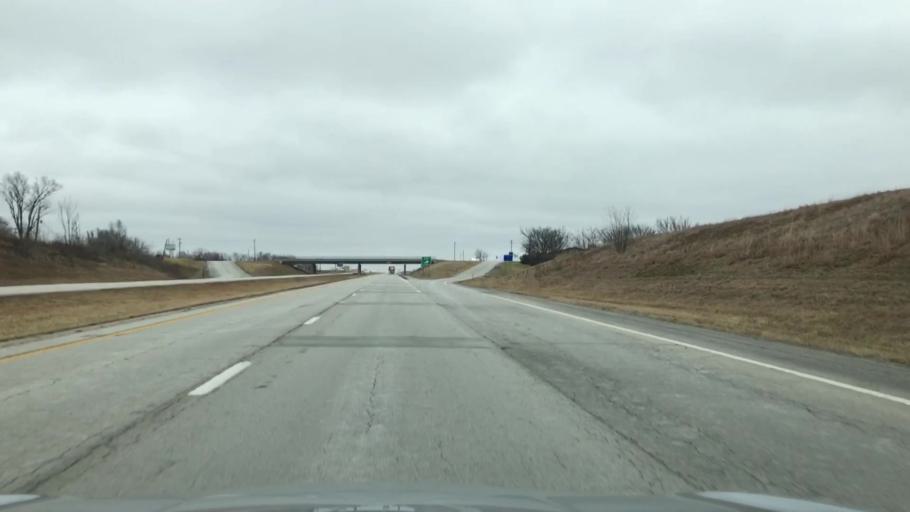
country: US
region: Missouri
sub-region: Caldwell County
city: Hamilton
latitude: 39.7334
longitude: -94.0049
